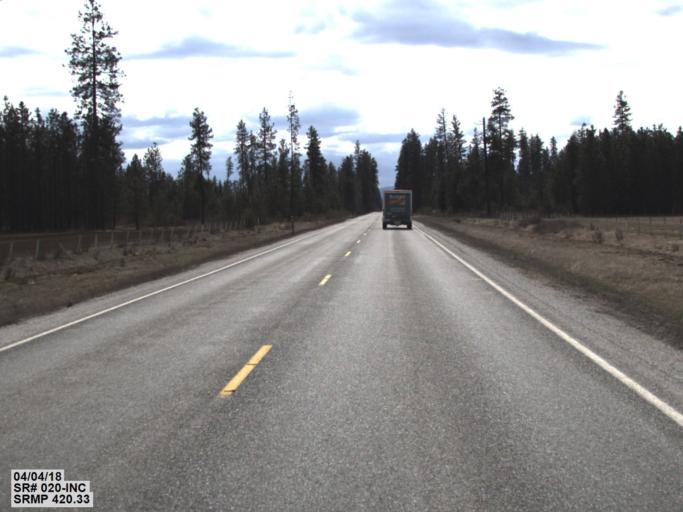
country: US
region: Washington
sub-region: Pend Oreille County
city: Newport
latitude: 48.3201
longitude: -117.2939
